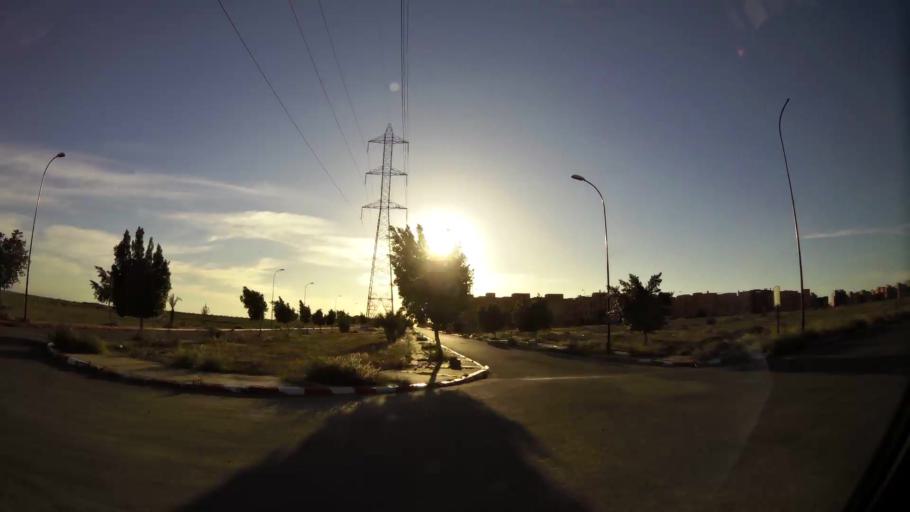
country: MA
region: Marrakech-Tensift-Al Haouz
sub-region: Marrakech
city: Marrakesh
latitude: 31.7429
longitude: -8.1137
